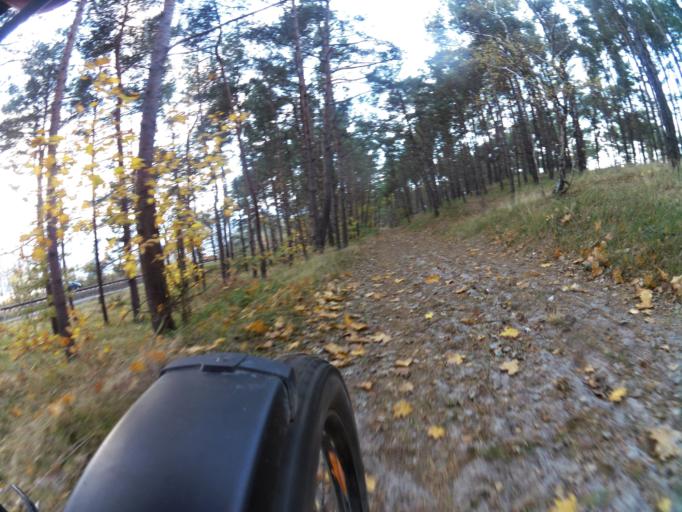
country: PL
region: Pomeranian Voivodeship
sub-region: Powiat pucki
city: Jastarnia
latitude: 54.7218
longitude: 18.6201
